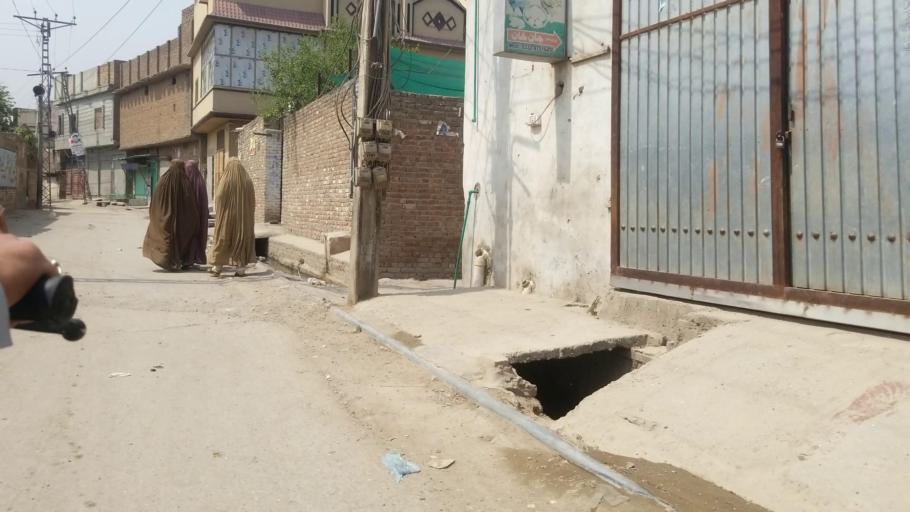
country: PK
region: Khyber Pakhtunkhwa
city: Peshawar
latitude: 33.9870
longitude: 71.5408
